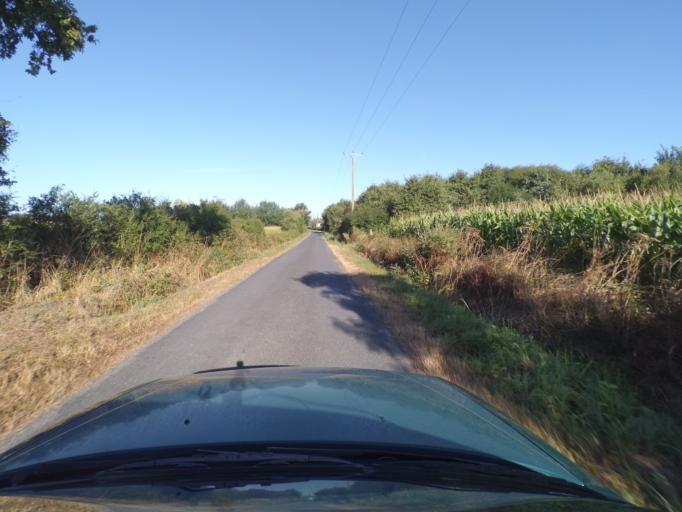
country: FR
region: Pays de la Loire
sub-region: Departement de la Loire-Atlantique
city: Le Bignon
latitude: 47.0905
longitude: -1.4686
